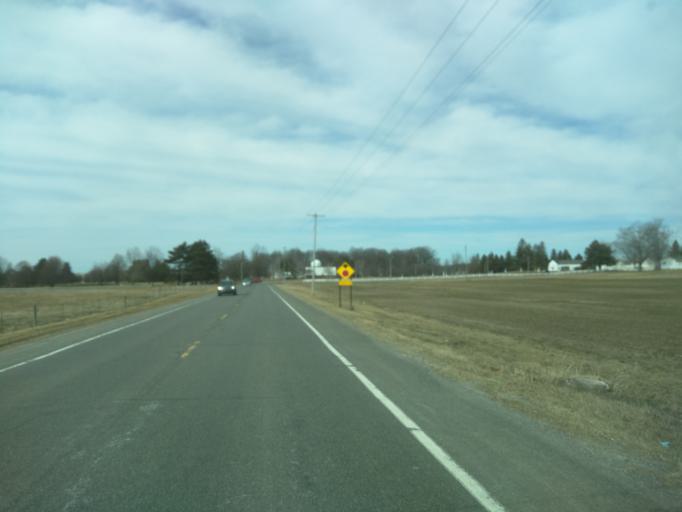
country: US
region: Michigan
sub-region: Ingham County
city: East Lansing
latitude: 42.7027
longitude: -84.4840
